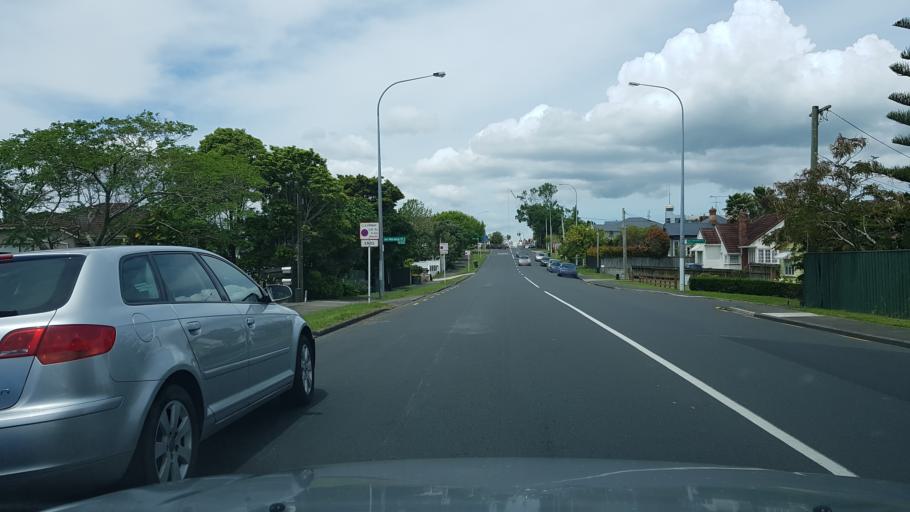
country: NZ
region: Auckland
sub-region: Auckland
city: North Shore
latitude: -36.8073
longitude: 174.7255
